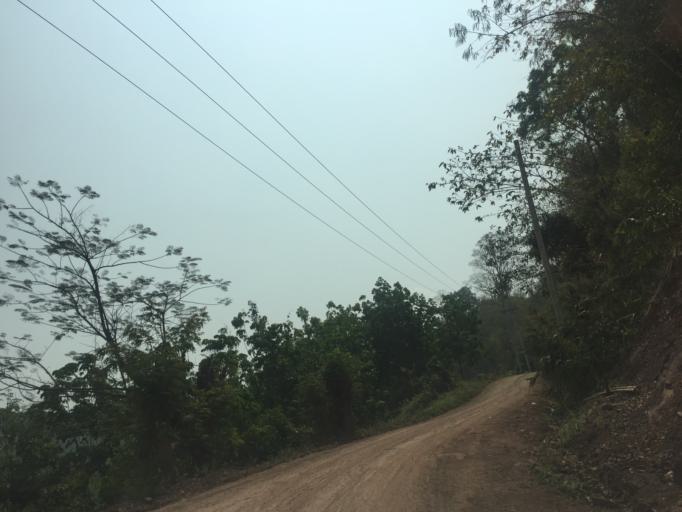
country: LA
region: Loungnamtha
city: Muang Nale
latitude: 20.2999
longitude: 101.6609
